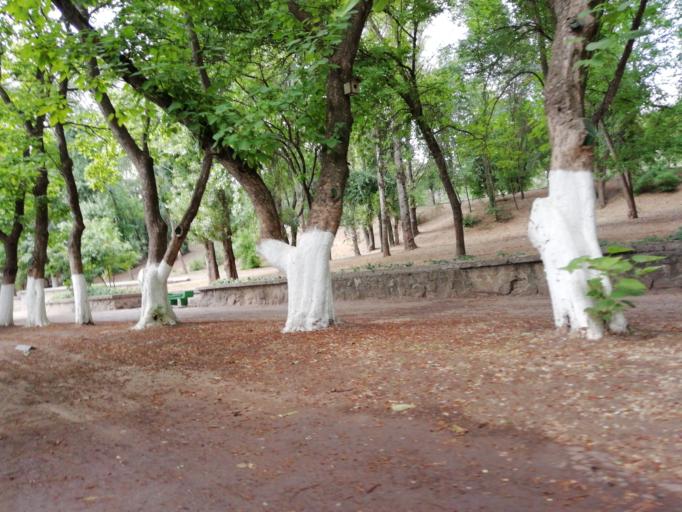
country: RU
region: Rostov
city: Severnyy
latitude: 47.2777
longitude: 39.7090
